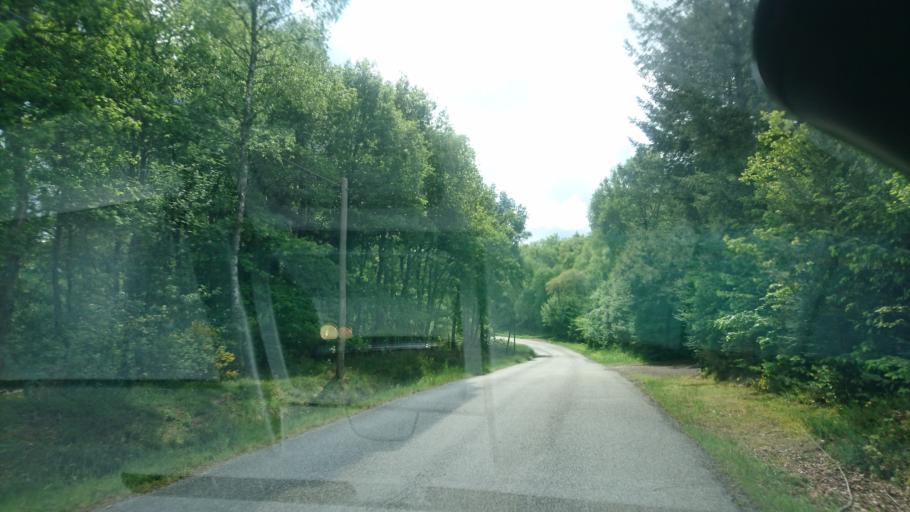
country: FR
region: Limousin
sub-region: Departement de la Haute-Vienne
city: Peyrat-le-Chateau
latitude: 45.7886
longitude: 1.8884
